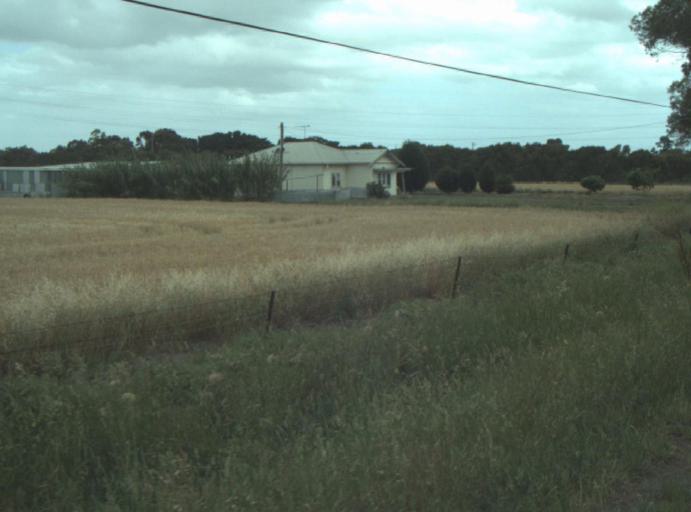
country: AU
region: Victoria
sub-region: Greater Geelong
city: Leopold
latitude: -38.1745
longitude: 144.4210
